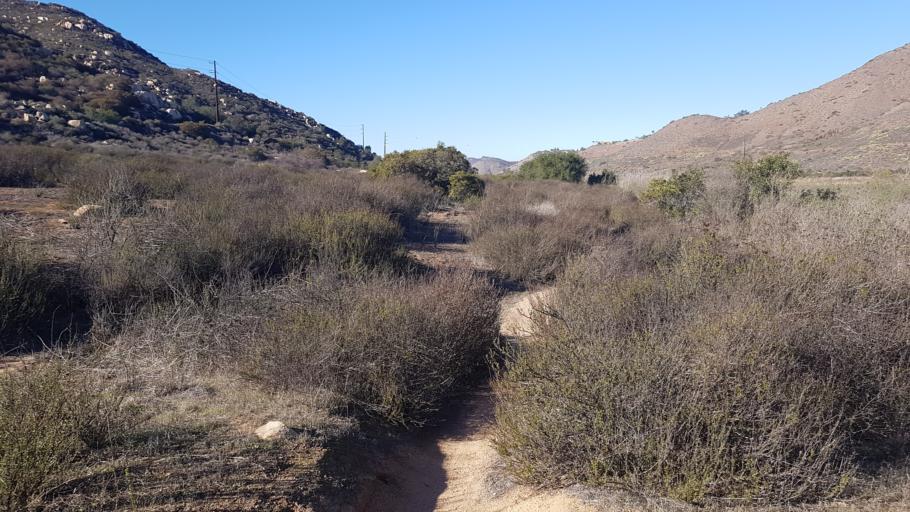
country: US
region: California
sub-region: San Diego County
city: Escondido
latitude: 33.0511
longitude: -117.0897
